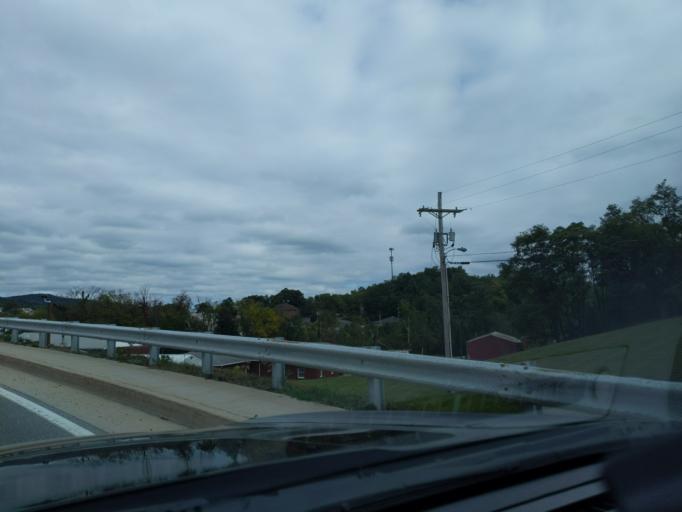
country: US
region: Pennsylvania
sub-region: Blair County
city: Lakemont
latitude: 40.4892
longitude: -78.4166
